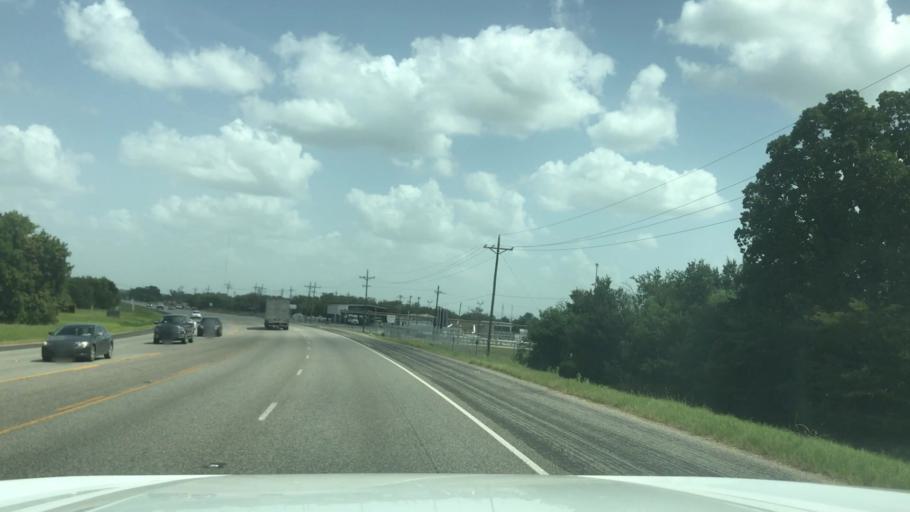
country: US
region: Texas
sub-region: Robertson County
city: Hearne
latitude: 30.8607
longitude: -96.5796
